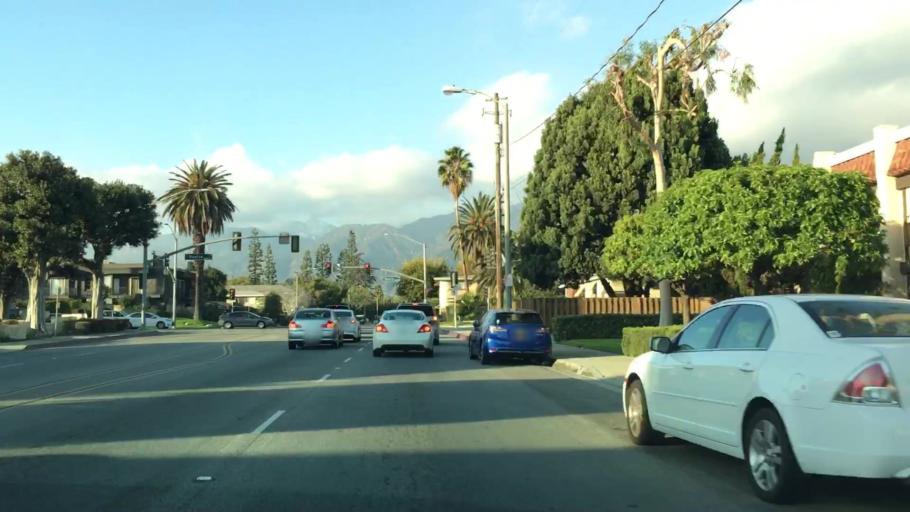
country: US
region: California
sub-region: Los Angeles County
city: Temple City
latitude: 34.1240
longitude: -118.0643
